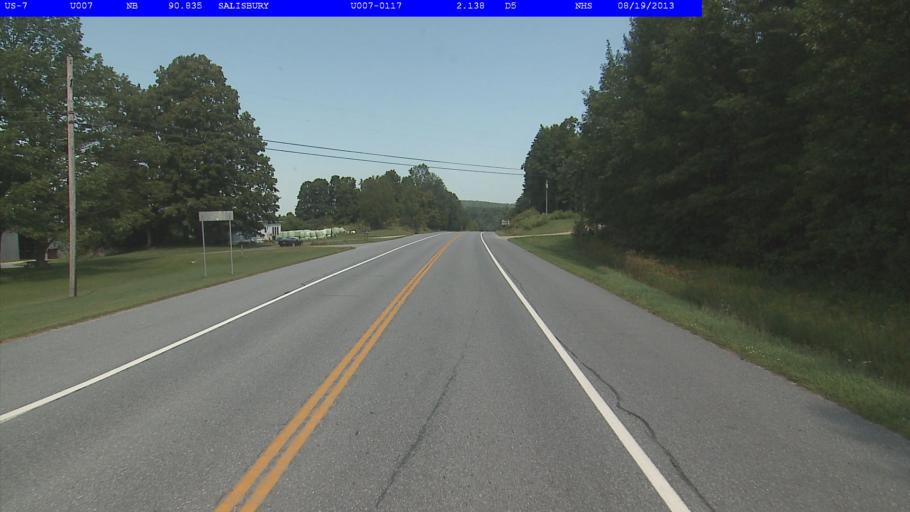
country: US
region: Vermont
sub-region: Addison County
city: Middlebury (village)
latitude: 43.9227
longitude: -73.1112
